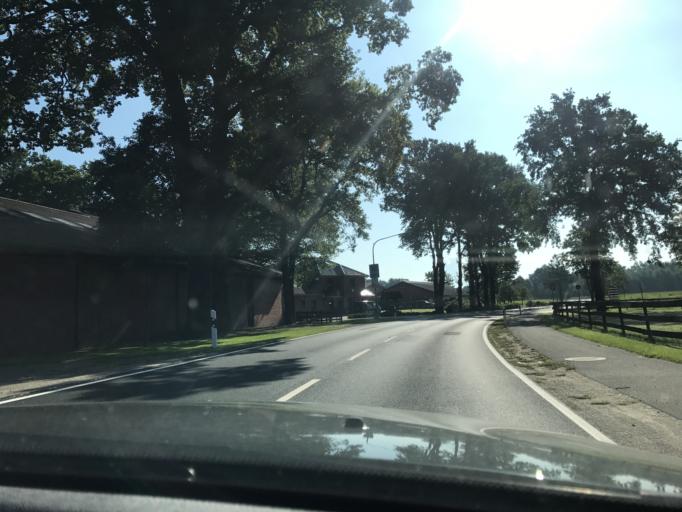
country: DE
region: Lower Saxony
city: Bawinkel
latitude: 52.6594
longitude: 7.4214
